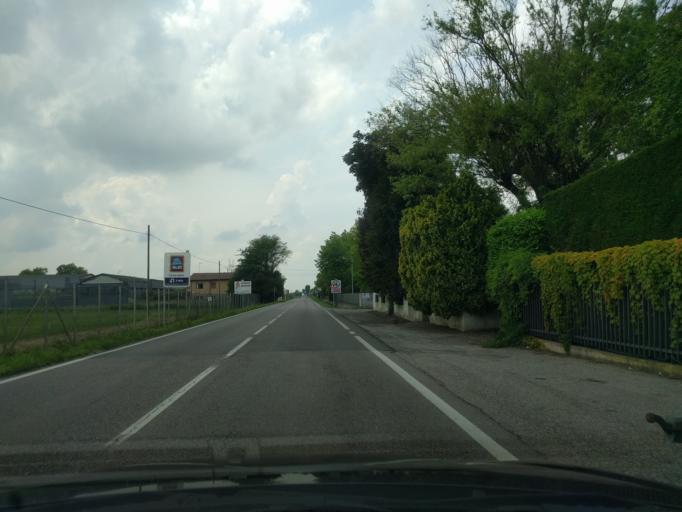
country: IT
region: Veneto
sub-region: Provincia di Rovigo
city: Lendinara
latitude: 45.0885
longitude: 11.5868
